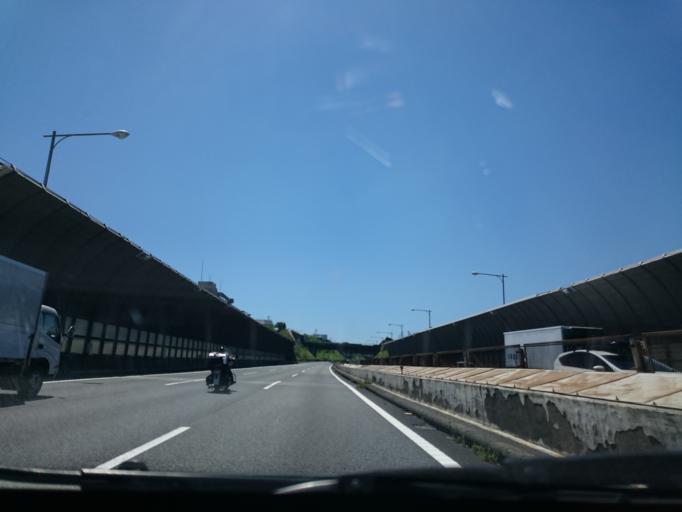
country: JP
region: Kanagawa
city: Hadano
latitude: 35.3676
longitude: 139.2603
